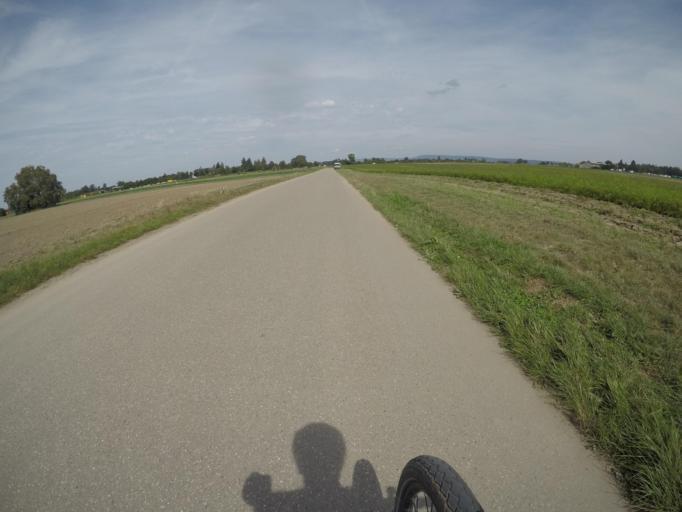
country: DE
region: Baden-Wuerttemberg
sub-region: Karlsruhe Region
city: Neulussheim
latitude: 49.2868
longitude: 8.5320
